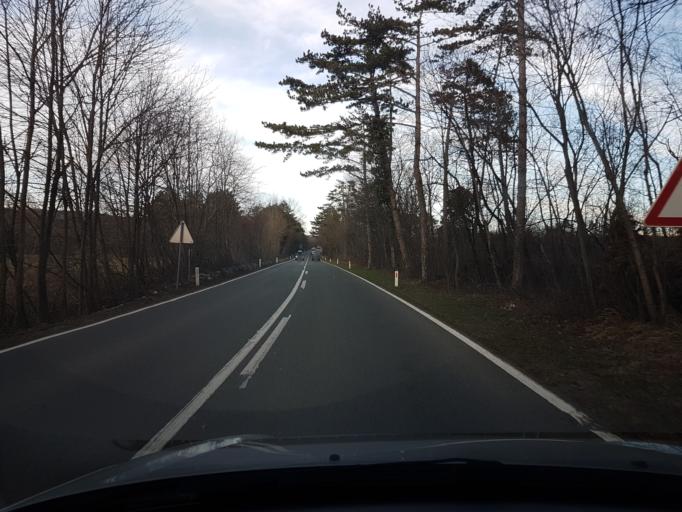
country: SI
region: Sezana
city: Sezana
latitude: 45.6578
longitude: 13.8961
